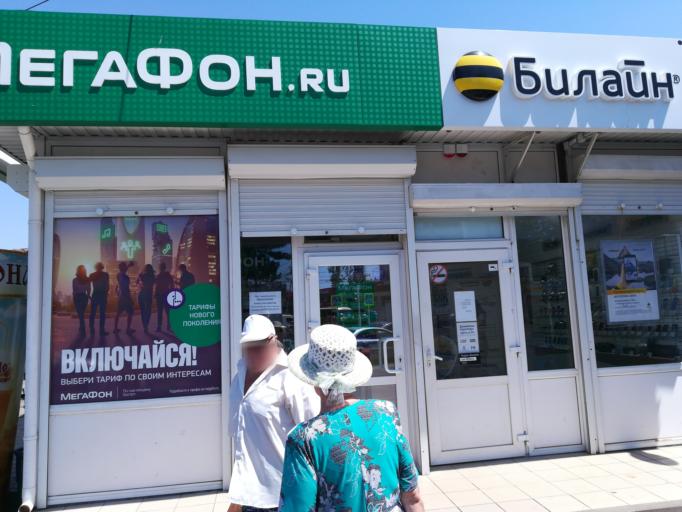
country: RU
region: Krasnodarskiy
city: Anapa
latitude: 44.8979
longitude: 37.3239
